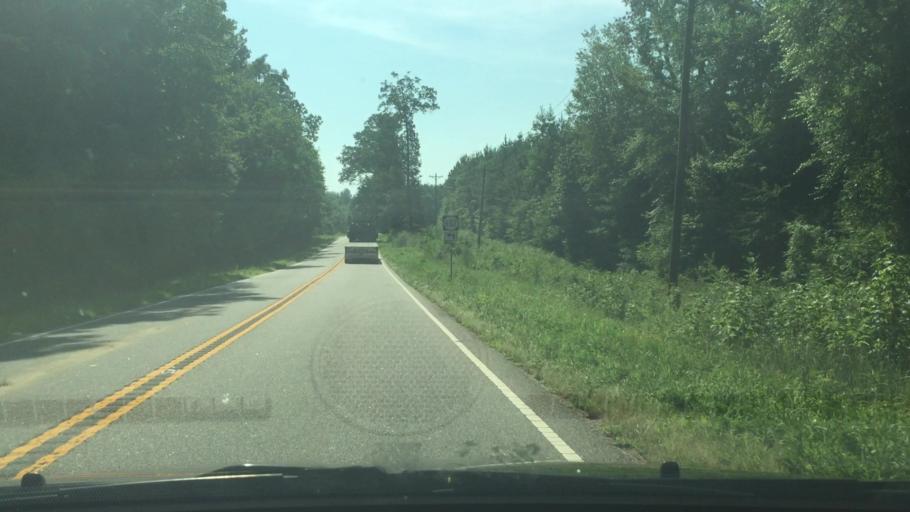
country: US
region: Virginia
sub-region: Sussex County
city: Sussex
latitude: 37.0133
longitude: -77.2775
